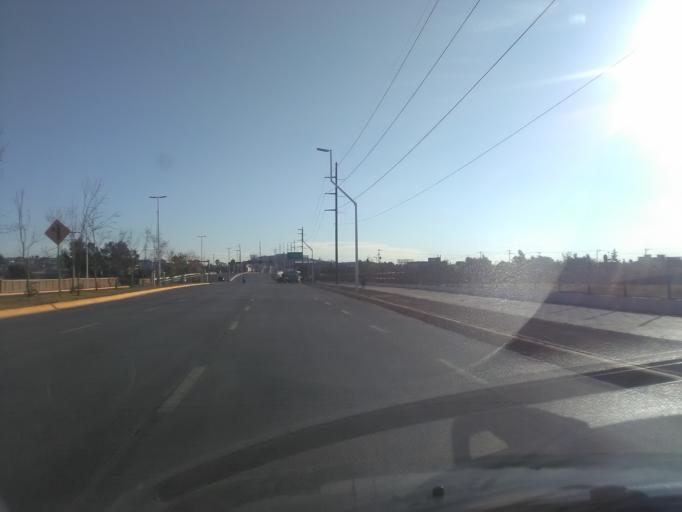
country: MX
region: Durango
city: Victoria de Durango
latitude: 24.0026
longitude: -104.6978
